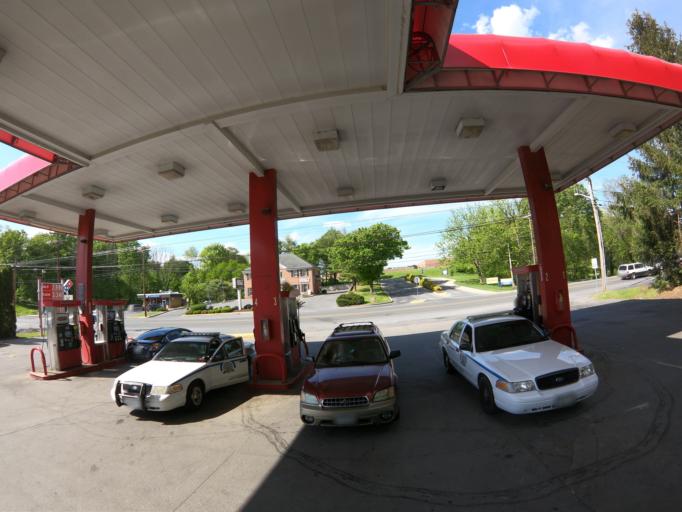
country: US
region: West Virginia
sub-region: Jefferson County
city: Shepherdstown
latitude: 39.4331
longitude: -77.8132
